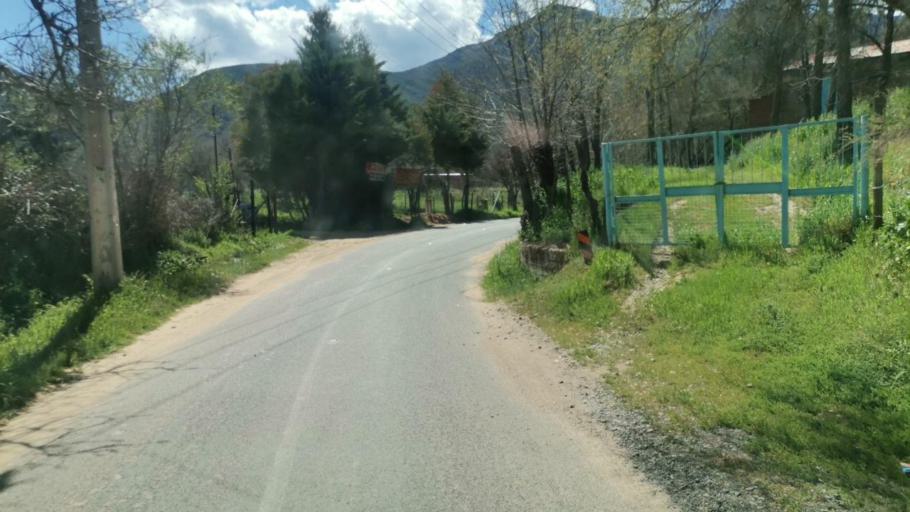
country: CL
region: Valparaiso
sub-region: Provincia de Marga Marga
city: Limache
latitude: -33.1740
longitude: -71.1667
